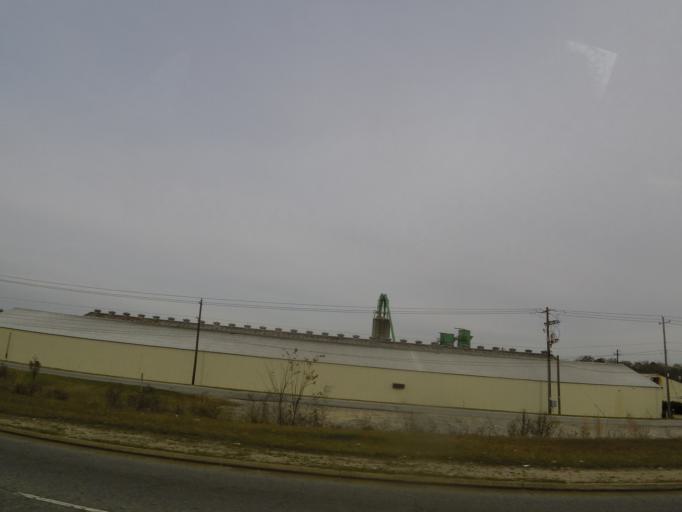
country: US
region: Georgia
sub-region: Decatur County
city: Bainbridge
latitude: 30.9115
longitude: -84.5835
